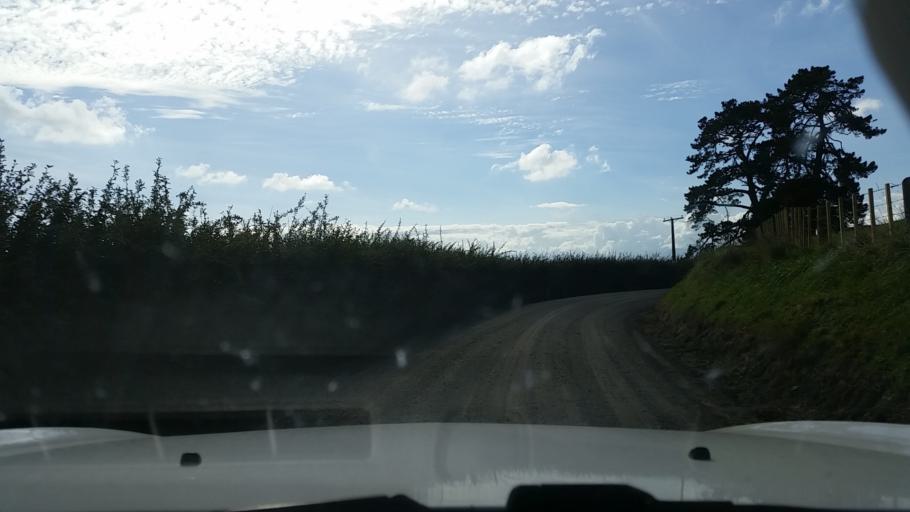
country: NZ
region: Waikato
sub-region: Matamata-Piako District
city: Matamata
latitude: -37.8188
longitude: 175.6439
